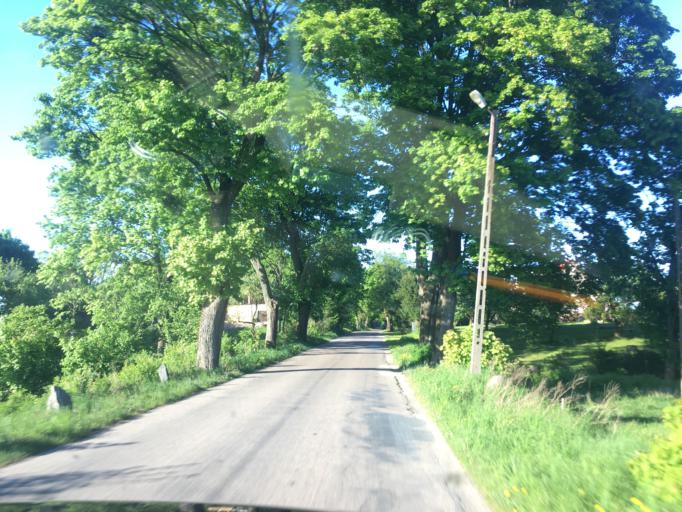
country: PL
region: Warmian-Masurian Voivodeship
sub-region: Powiat piski
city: Ruciane-Nida
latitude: 53.6786
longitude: 21.4946
